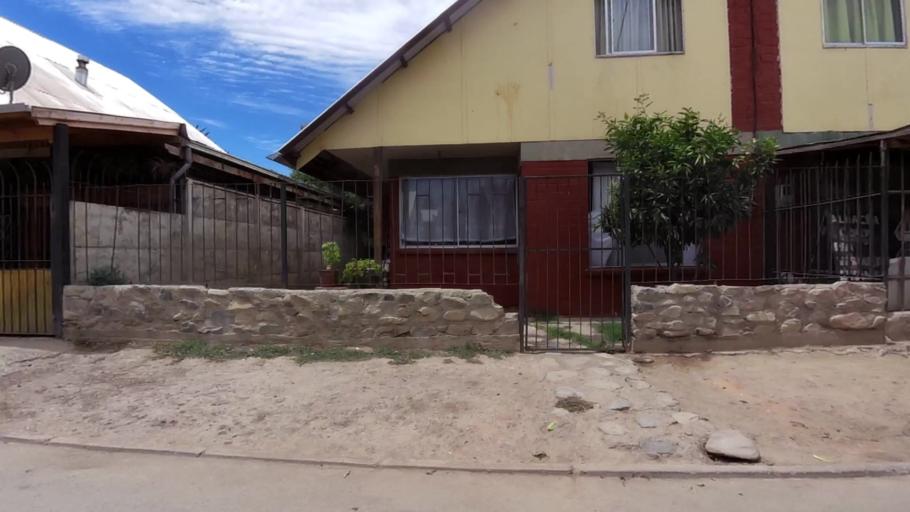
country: CL
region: O'Higgins
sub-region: Provincia de Cachapoal
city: Graneros
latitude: -34.0718
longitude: -70.7368
